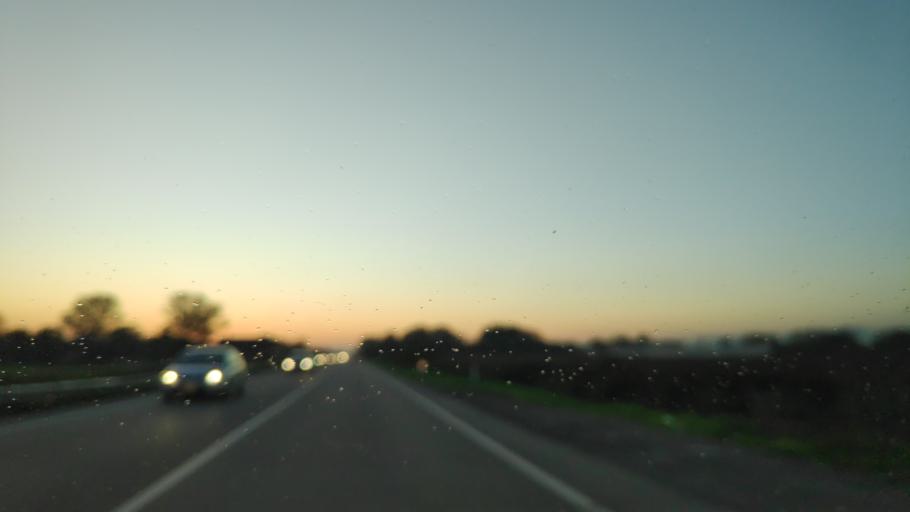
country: IT
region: Lombardy
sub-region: Citta metropolitana di Milano
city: Gaggiano
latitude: 45.4056
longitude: 9.0199
